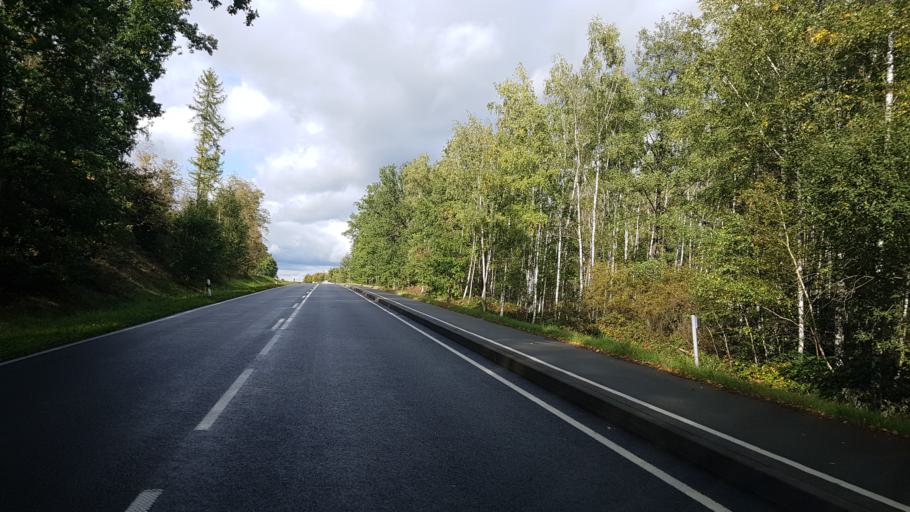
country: DE
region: Saxony
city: Dahlen
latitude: 51.3789
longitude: 12.9926
